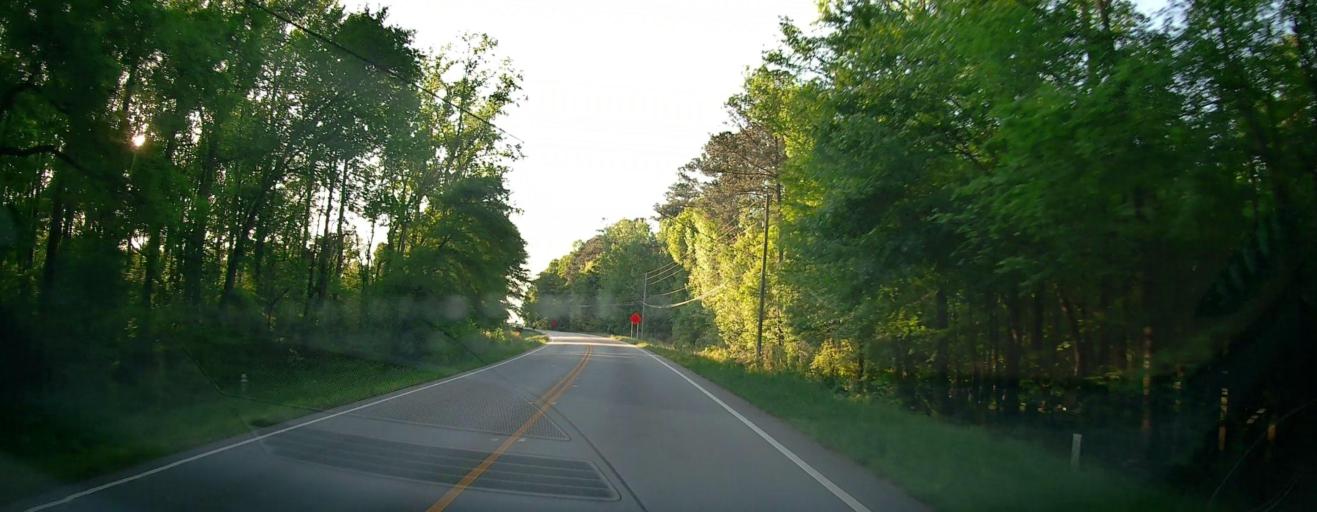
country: US
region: Georgia
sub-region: Newton County
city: Covington
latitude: 33.5863
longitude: -83.7849
